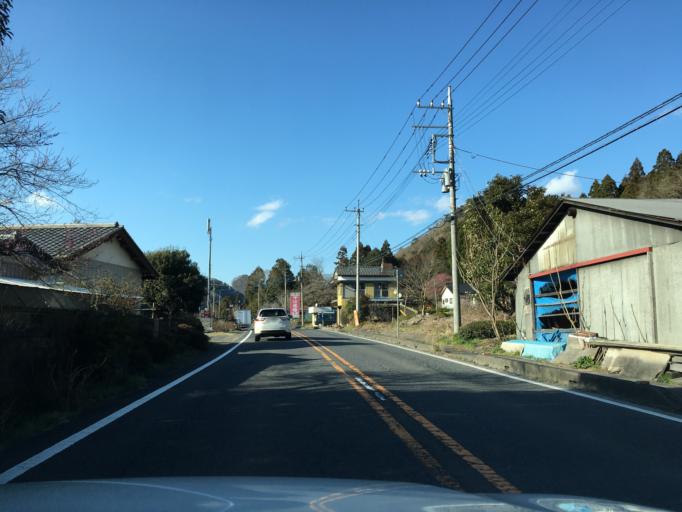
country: JP
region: Ibaraki
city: Daigo
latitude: 36.6759
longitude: 140.3904
